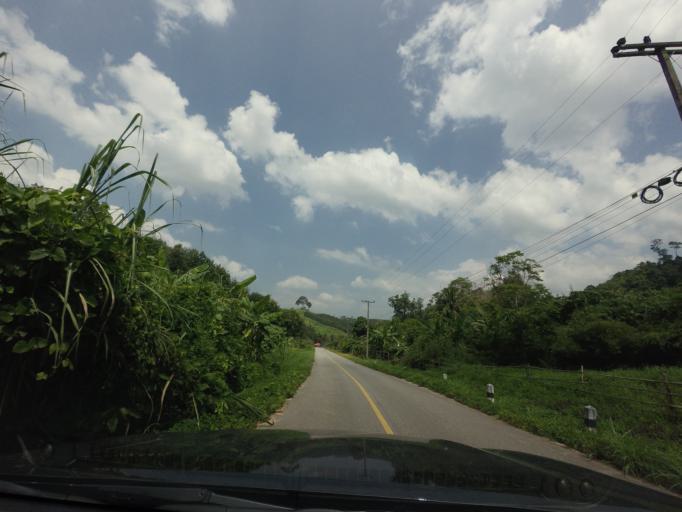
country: TH
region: Loei
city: Na Haeo
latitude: 17.6611
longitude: 100.9232
